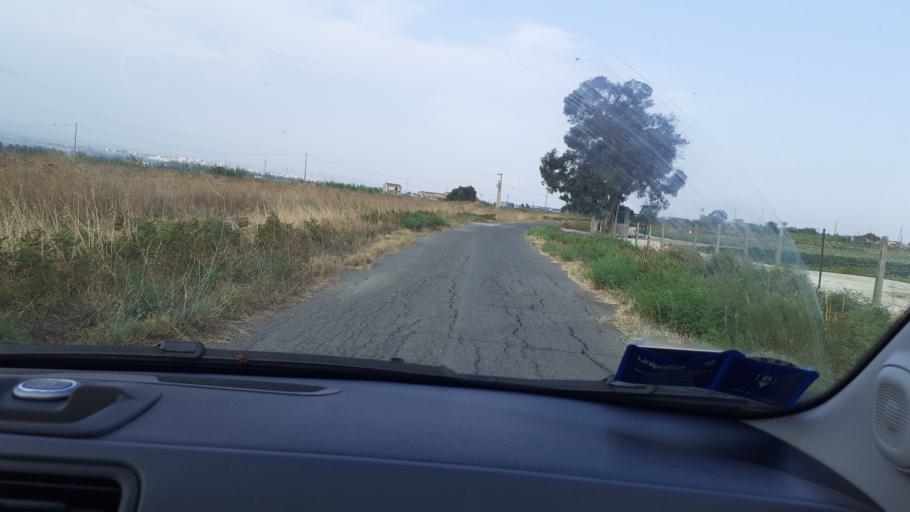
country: IT
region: Sicily
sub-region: Catania
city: Catania
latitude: 37.4308
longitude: 15.0148
